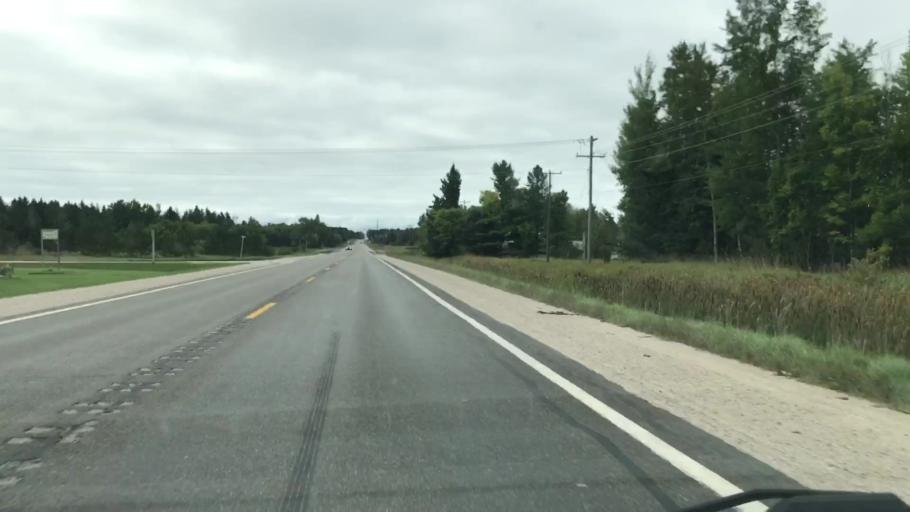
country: US
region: Michigan
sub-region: Luce County
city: Newberry
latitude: 46.1376
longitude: -85.5713
